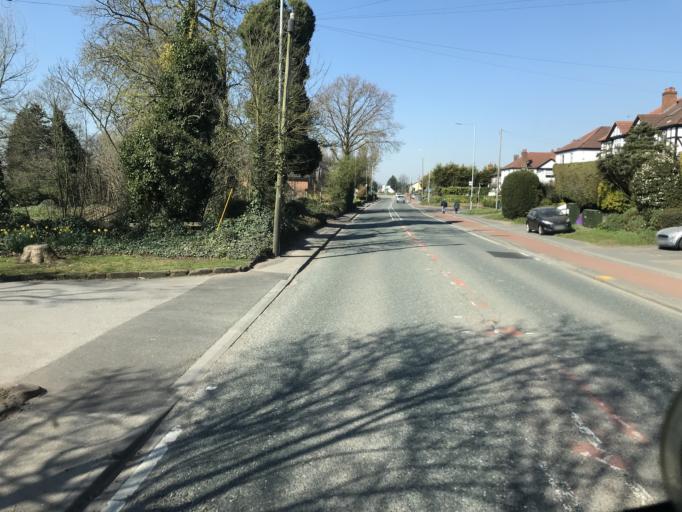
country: GB
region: England
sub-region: Cheshire West and Chester
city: Guilden Sutton
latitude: 53.1861
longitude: -2.8481
